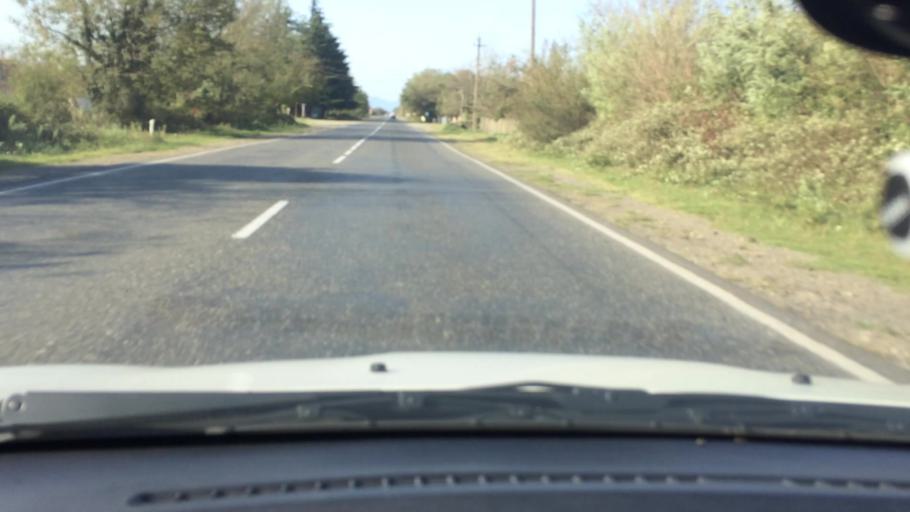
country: GE
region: Imereti
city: Tsqaltubo
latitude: 42.2154
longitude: 42.5661
